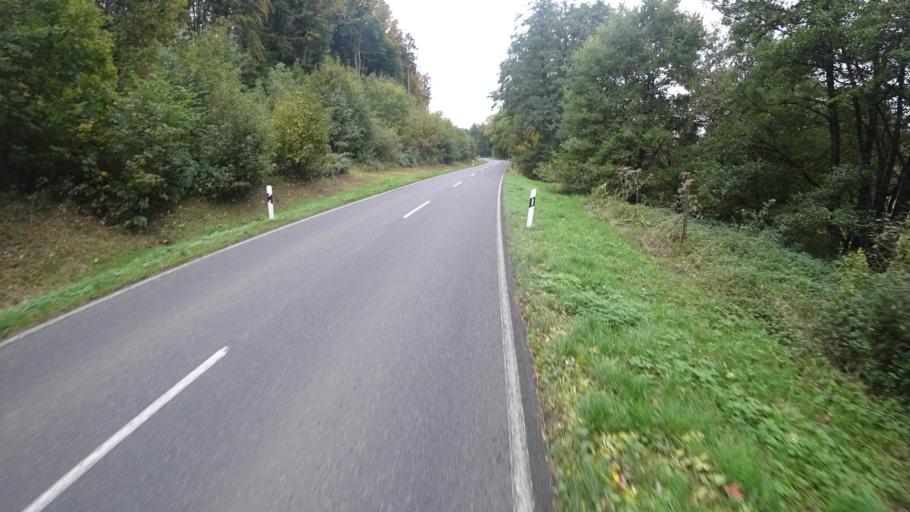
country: DE
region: Rheinland-Pfalz
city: Oberhaid
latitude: 50.5152
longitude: 7.7303
